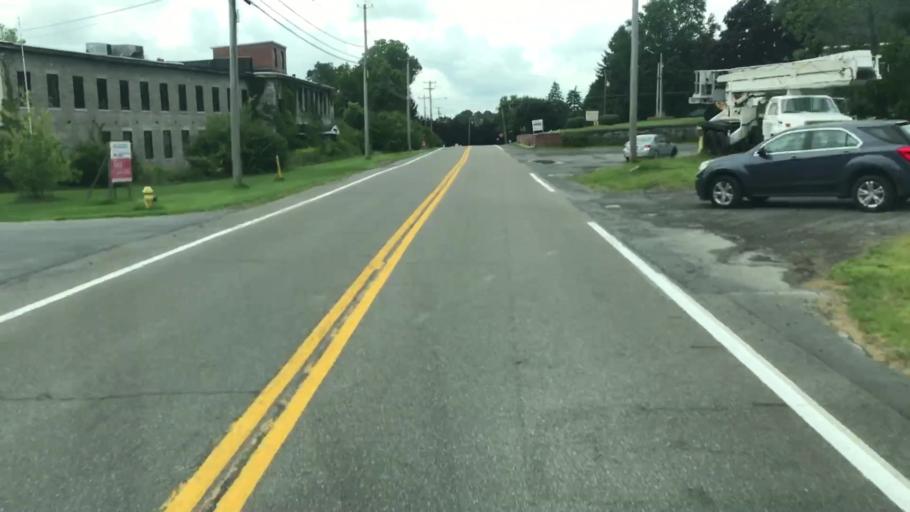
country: US
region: New York
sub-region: Onondaga County
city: Elbridge
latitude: 42.9919
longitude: -76.4550
